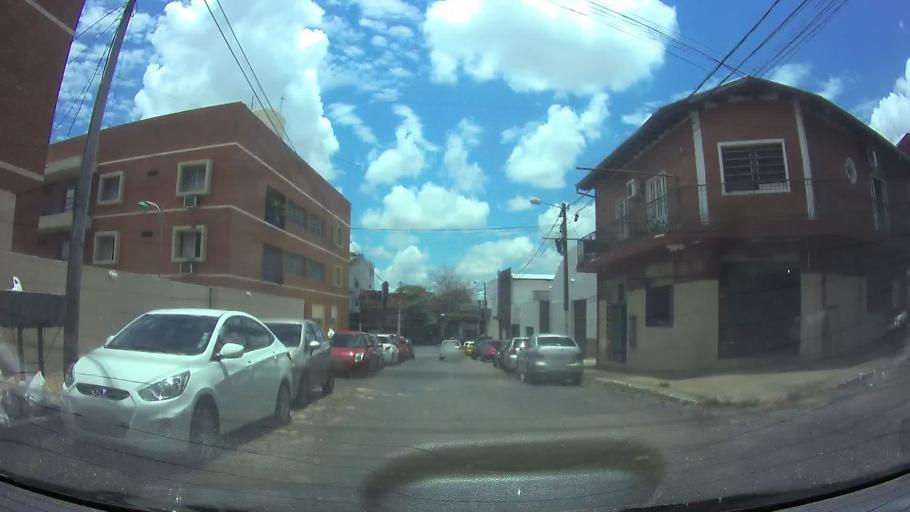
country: PY
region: Central
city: Lambare
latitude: -25.3107
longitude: -57.5926
